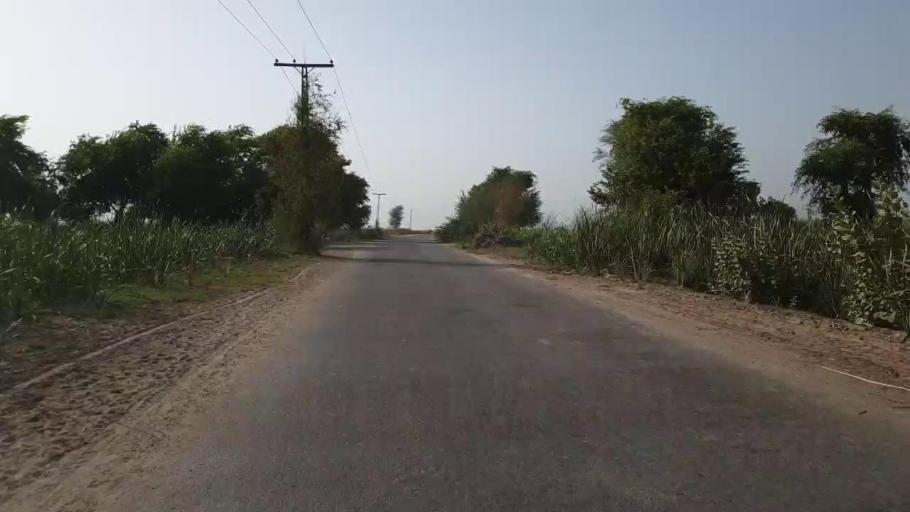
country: PK
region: Sindh
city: Jam Sahib
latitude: 26.3934
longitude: 68.8798
